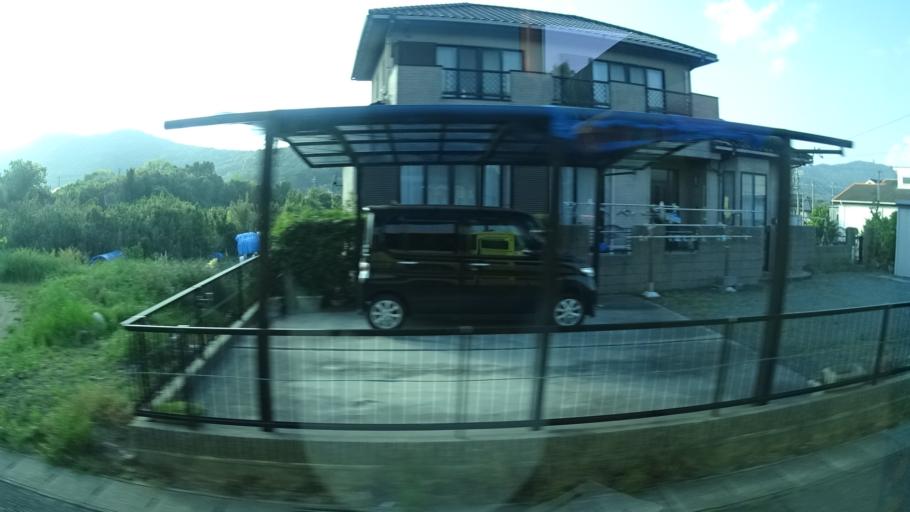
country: JP
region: Aichi
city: Tahara
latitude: 34.6625
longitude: 137.2562
